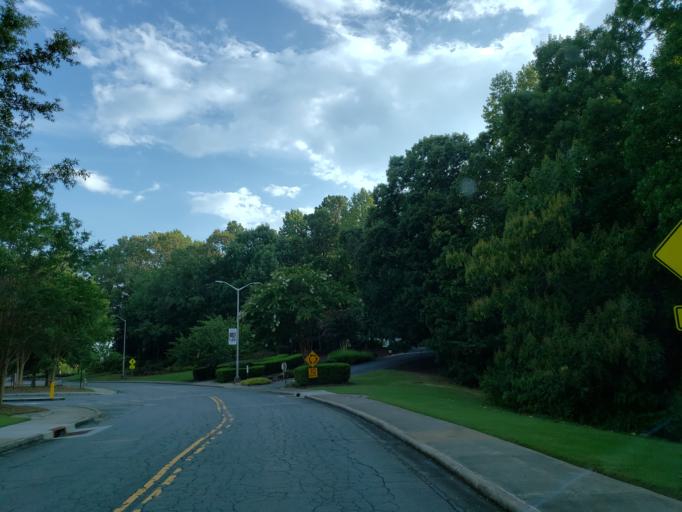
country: US
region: Georgia
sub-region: Cobb County
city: Kennesaw
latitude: 34.0428
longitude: -84.5844
